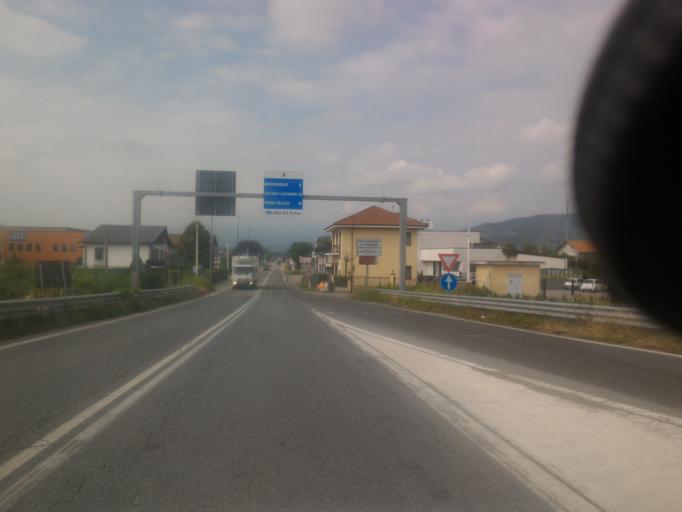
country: IT
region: Piedmont
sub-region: Provincia di Torino
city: Osasco
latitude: 44.8639
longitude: 7.3320
